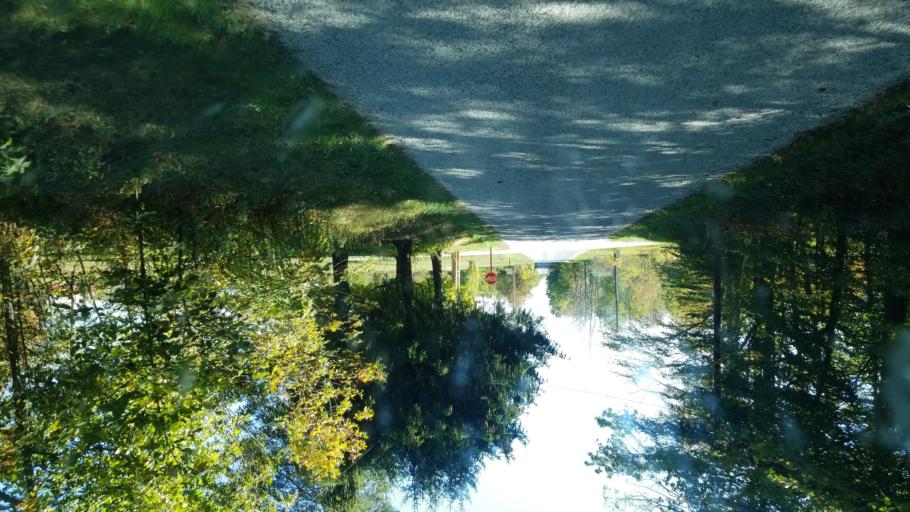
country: US
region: Ohio
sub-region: Wayne County
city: West Salem
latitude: 40.8934
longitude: -82.1738
